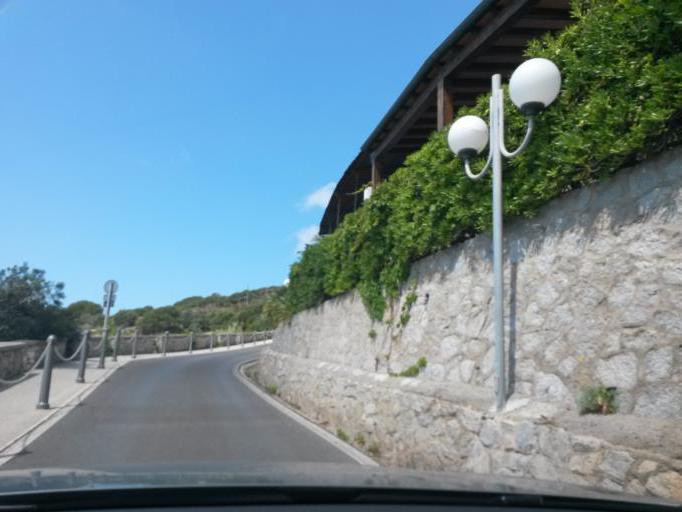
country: IT
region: Tuscany
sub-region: Provincia di Livorno
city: Campo nell'Elba
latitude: 42.7376
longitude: 10.1853
